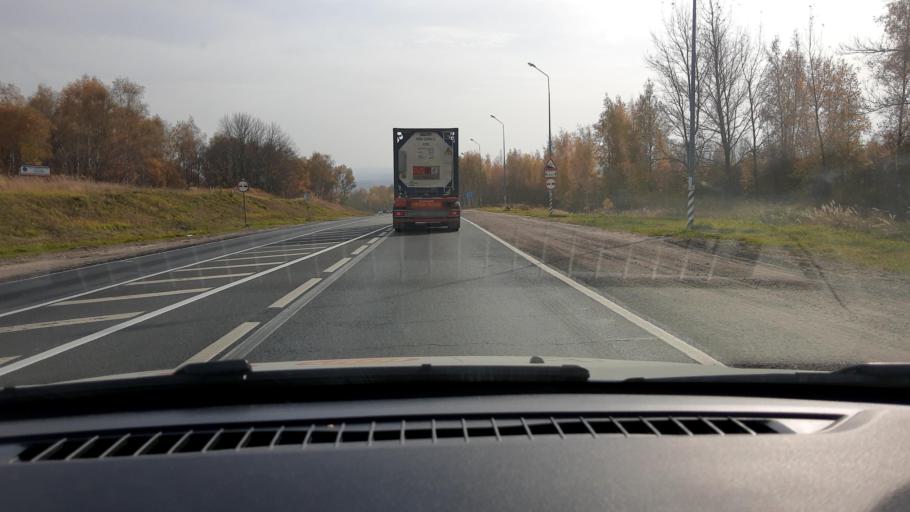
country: RU
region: Nizjnij Novgorod
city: Kstovo
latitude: 56.1090
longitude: 44.2859
